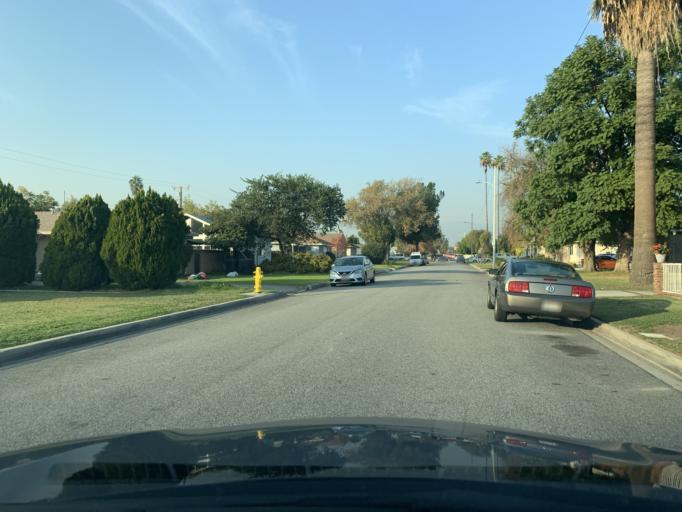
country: US
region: California
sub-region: Los Angeles County
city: Covina
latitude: 34.0938
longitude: -117.8911
